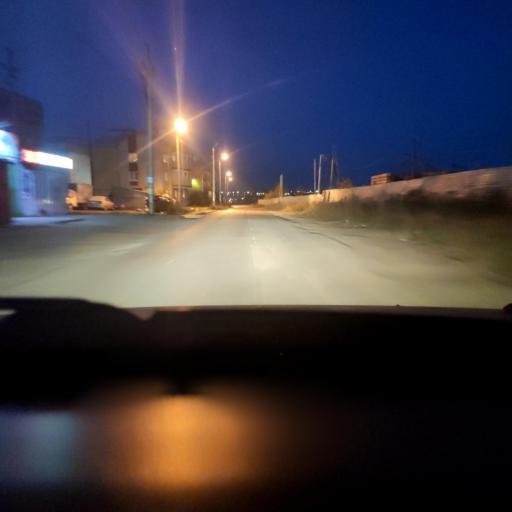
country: RU
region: Perm
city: Ferma
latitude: 57.8975
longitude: 56.3288
